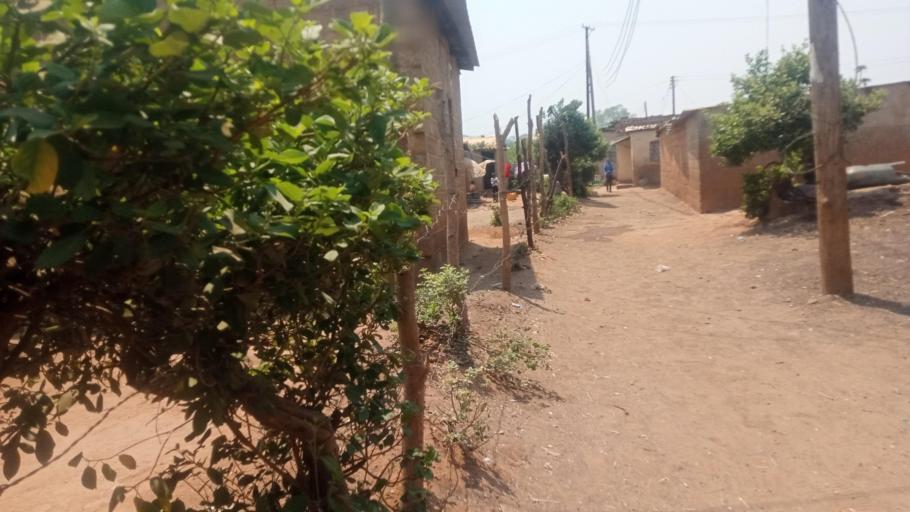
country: ZM
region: Lusaka
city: Lusaka
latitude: -15.4462
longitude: 28.3826
